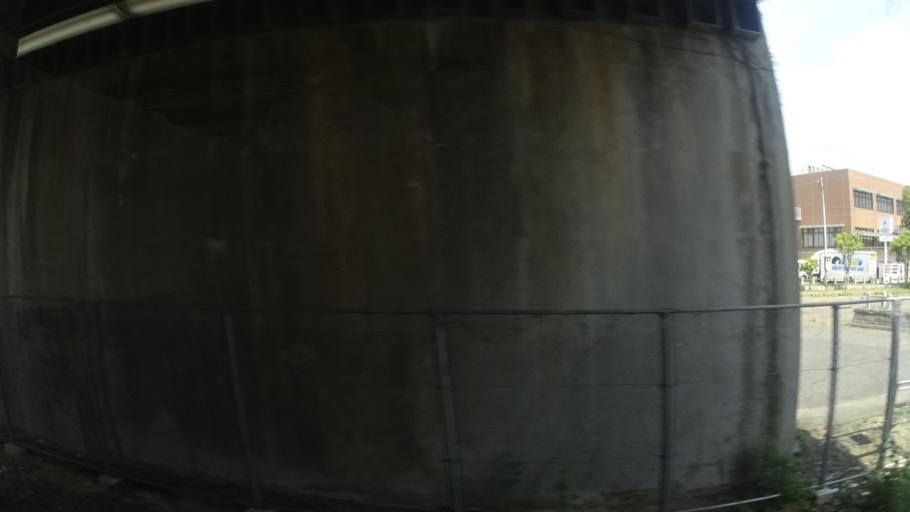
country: JP
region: Mie
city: Yokkaichi
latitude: 34.9540
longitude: 136.6225
